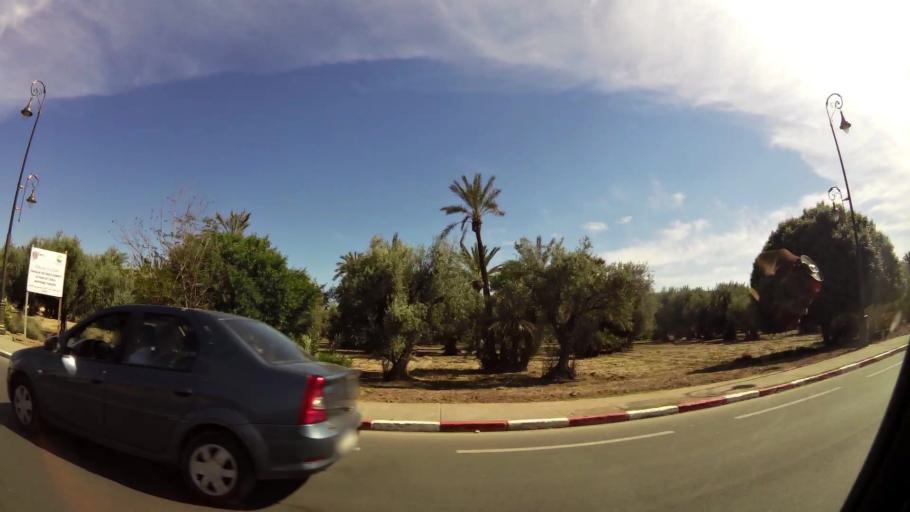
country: MA
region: Marrakech-Tensift-Al Haouz
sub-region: Marrakech
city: Marrakesh
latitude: 31.6463
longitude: -7.9756
